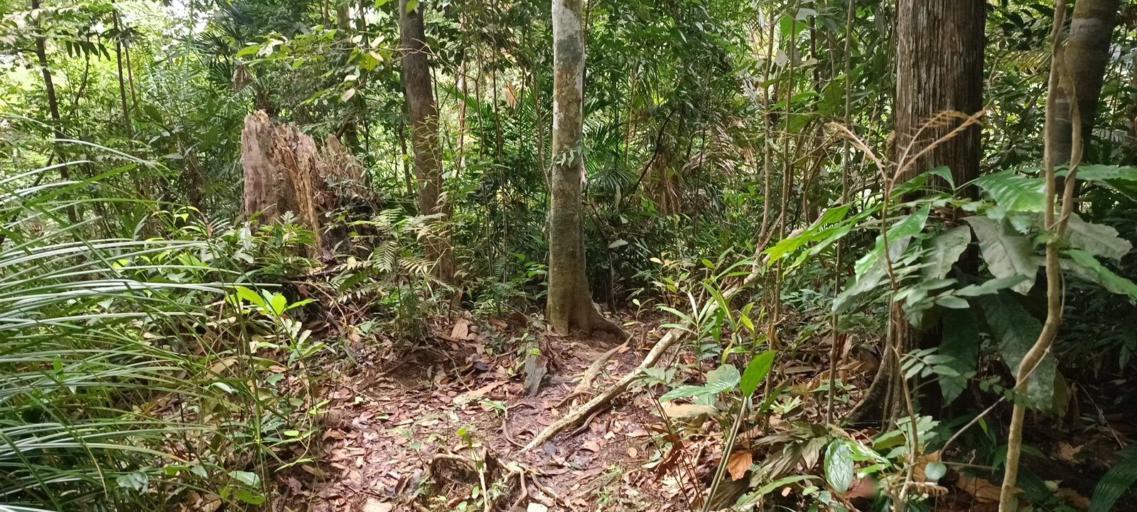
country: MY
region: Penang
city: Bukit Mertajam
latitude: 5.3626
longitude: 100.4822
